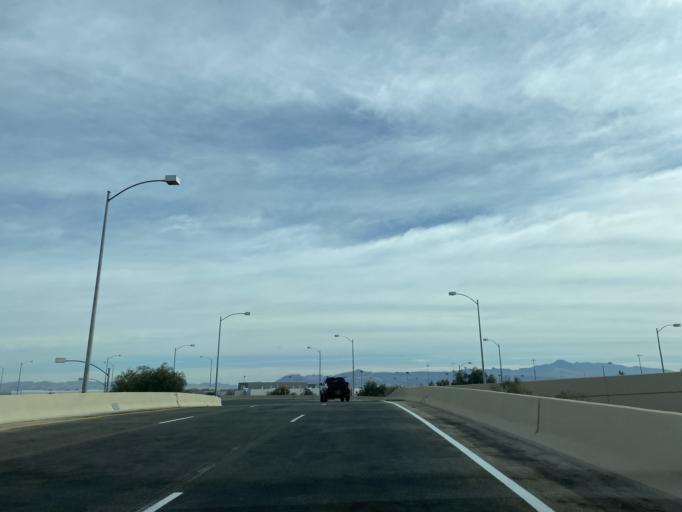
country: US
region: Nevada
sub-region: Clark County
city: Paradise
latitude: 36.0871
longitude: -115.1322
